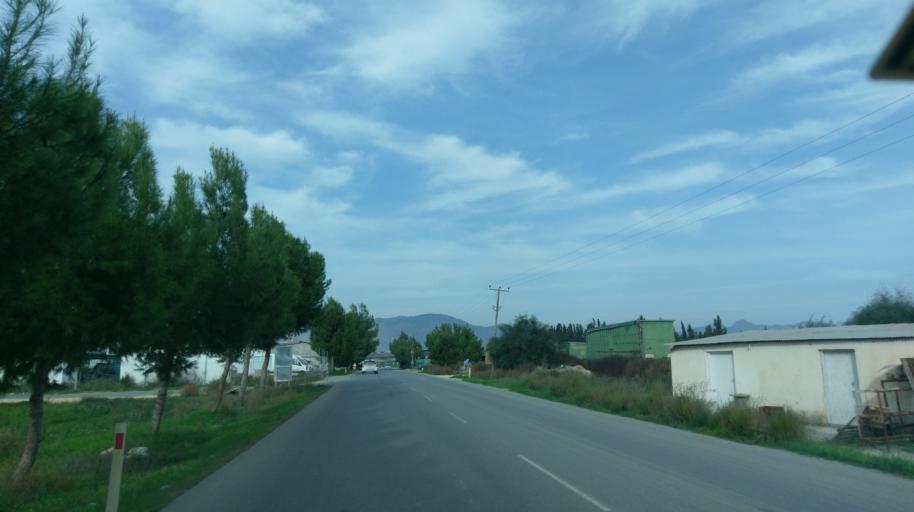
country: CY
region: Lefkosia
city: Mammari
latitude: 35.2103
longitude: 33.2776
